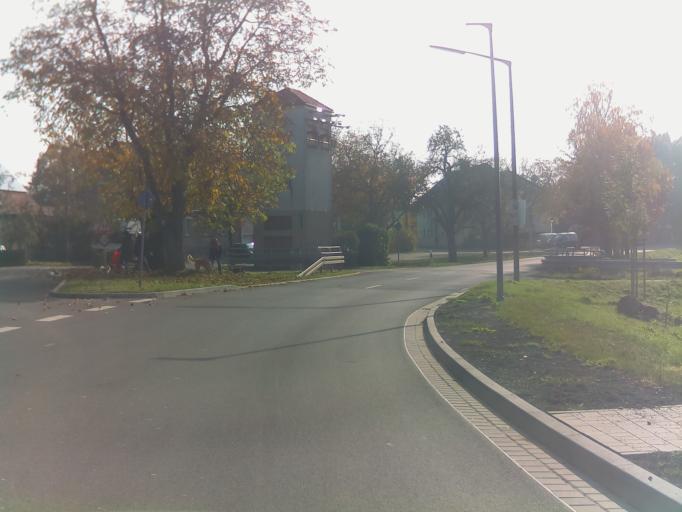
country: DE
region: Bavaria
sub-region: Regierungsbezirk Unterfranken
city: Biebelried
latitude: 49.7630
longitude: 10.0795
